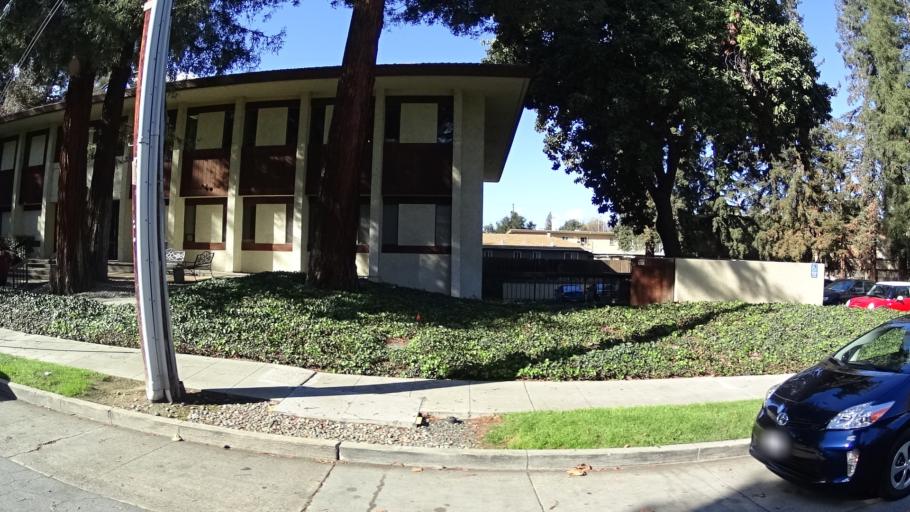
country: US
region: California
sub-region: Santa Clara County
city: Buena Vista
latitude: 37.3357
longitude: -121.9160
